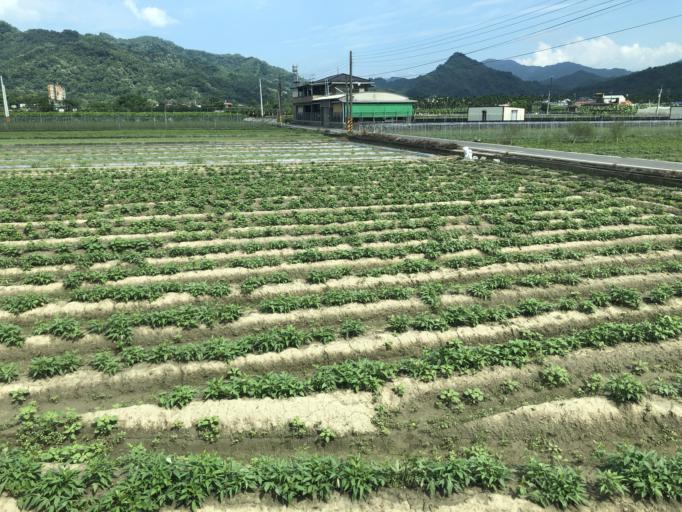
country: TW
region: Taiwan
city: Yujing
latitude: 22.9131
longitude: 120.5718
